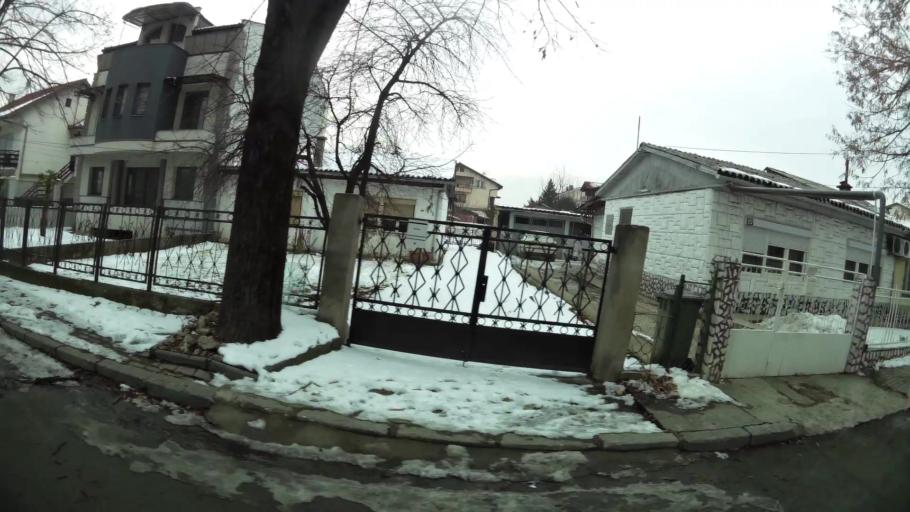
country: MK
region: Butel
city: Butel
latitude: 42.0332
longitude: 21.4439
